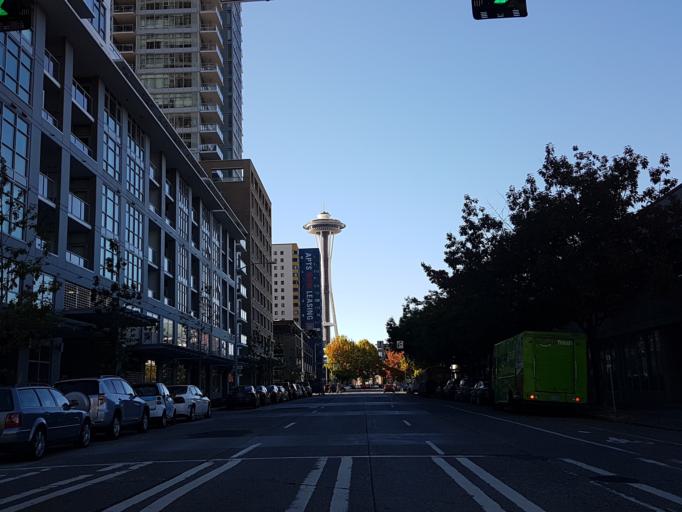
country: US
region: Washington
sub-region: King County
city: Seattle
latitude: 47.6168
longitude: -122.3423
